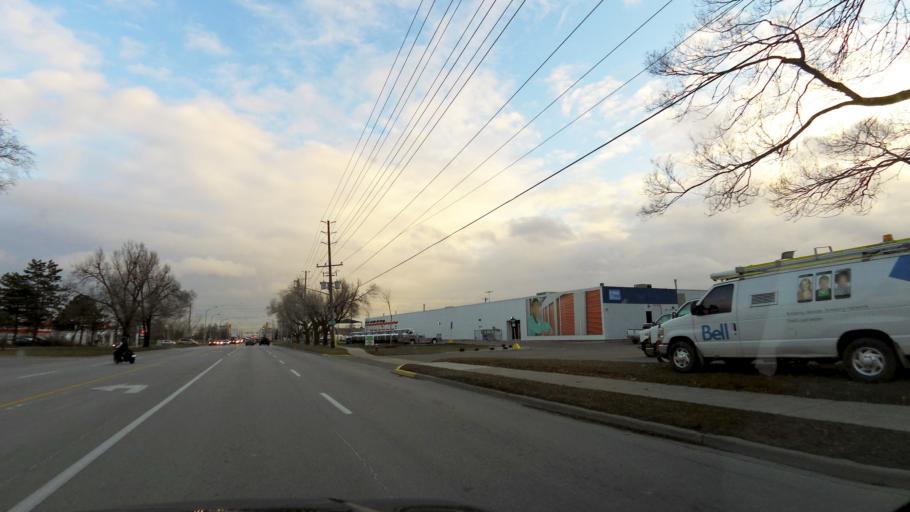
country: CA
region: Ontario
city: Brampton
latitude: 43.7182
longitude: -79.6854
